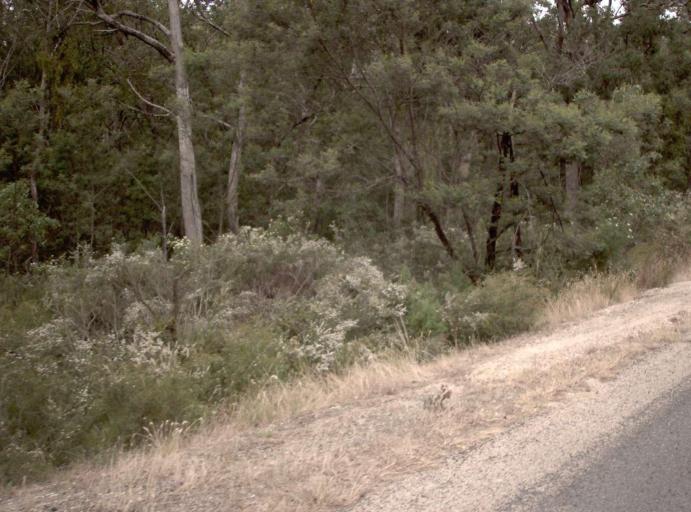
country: AU
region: Victoria
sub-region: East Gippsland
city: Lakes Entrance
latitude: -37.7224
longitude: 147.8788
